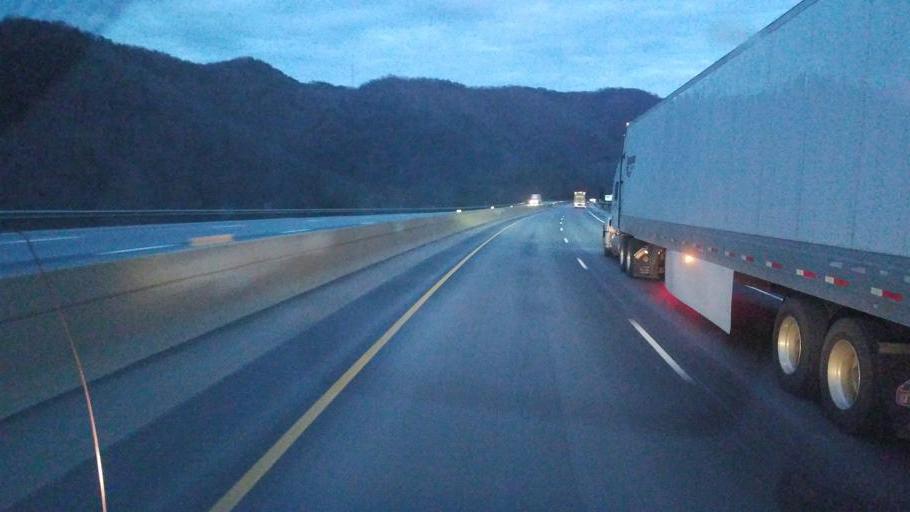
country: US
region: West Virginia
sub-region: Kanawha County
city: Montgomery
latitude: 38.1357
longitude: -81.4083
